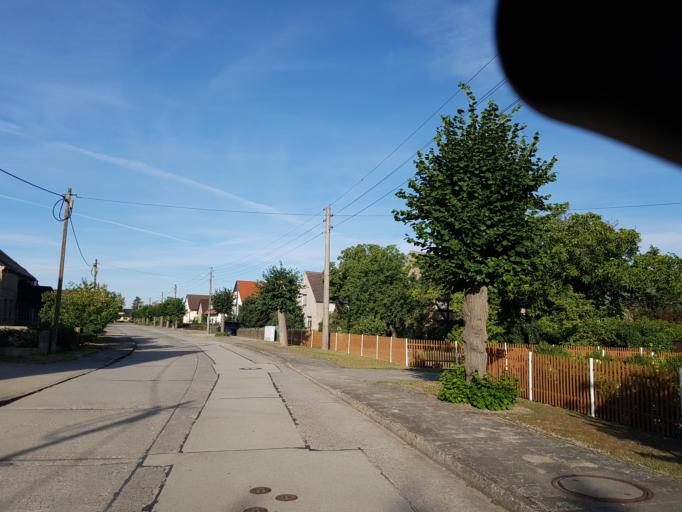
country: DE
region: Saxony
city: Nauwalde
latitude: 51.4450
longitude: 13.3663
